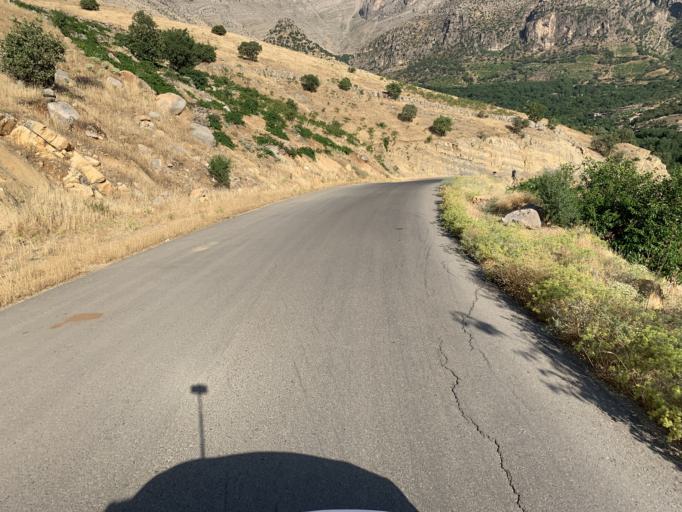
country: IQ
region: As Sulaymaniyah
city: Qeladize
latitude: 35.9943
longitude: 45.1943
